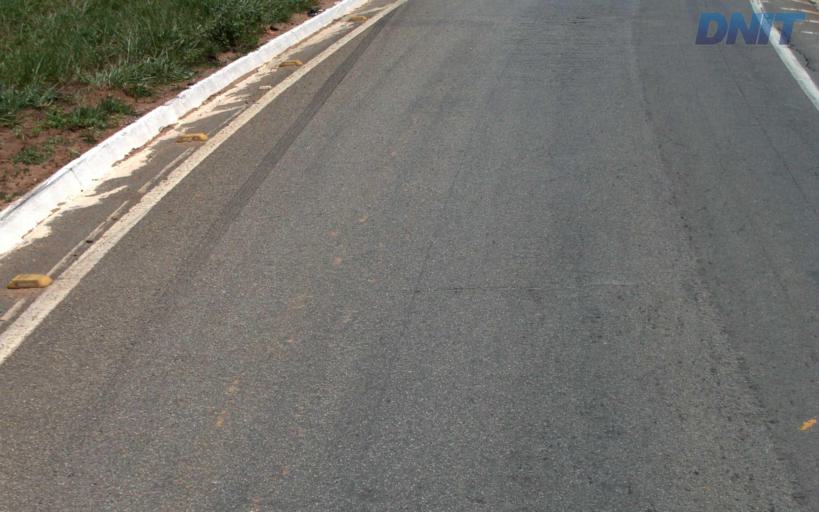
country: BR
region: Minas Gerais
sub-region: Governador Valadares
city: Governador Valadares
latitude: -18.8923
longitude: -42.0048
